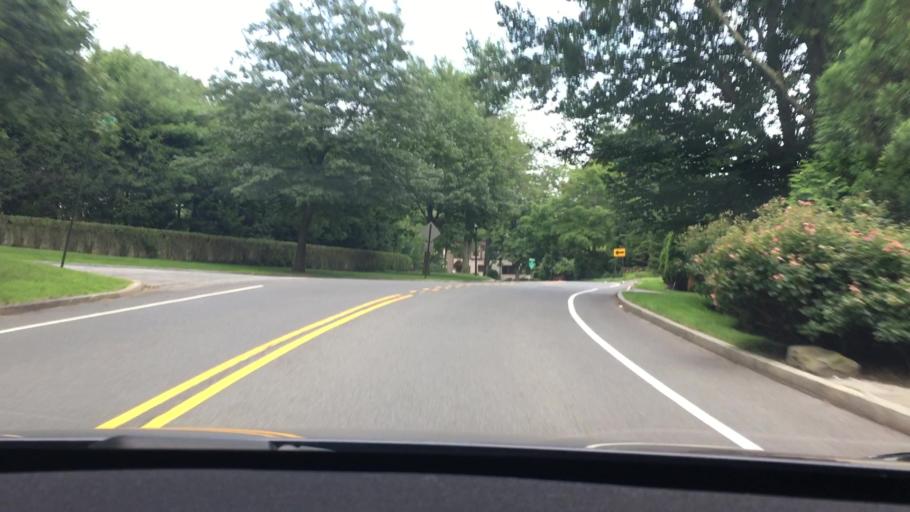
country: US
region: New York
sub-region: Westchester County
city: New Rochelle
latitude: 40.9312
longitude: -73.7829
